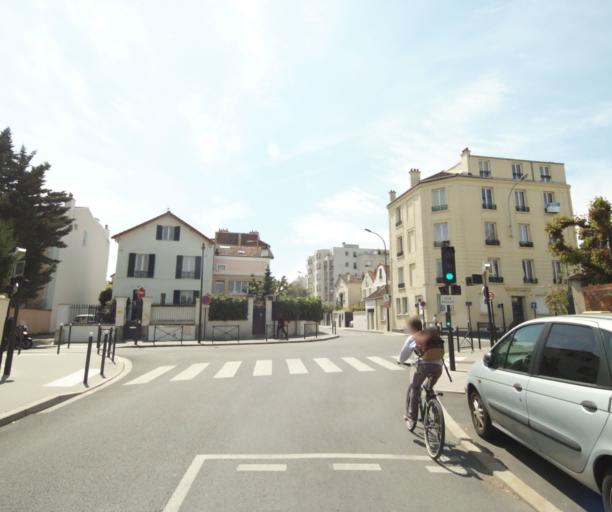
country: FR
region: Ile-de-France
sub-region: Departement des Hauts-de-Seine
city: Bois-Colombes
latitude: 48.9122
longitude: 2.2653
